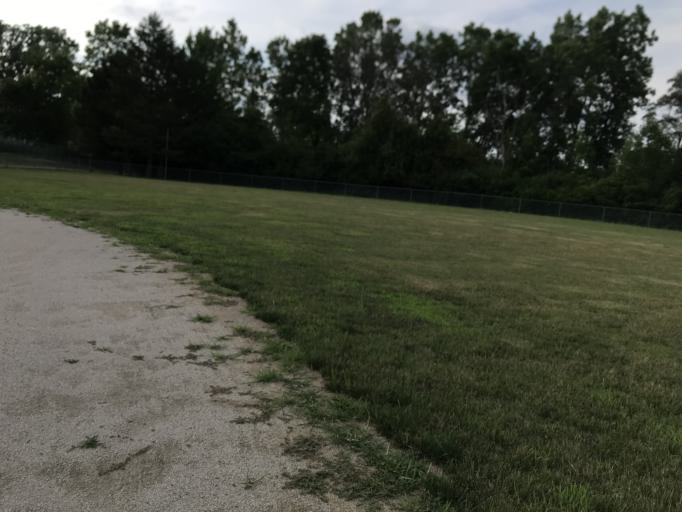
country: US
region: Michigan
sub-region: Oakland County
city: Farmington Hills
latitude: 42.4884
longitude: -83.3377
